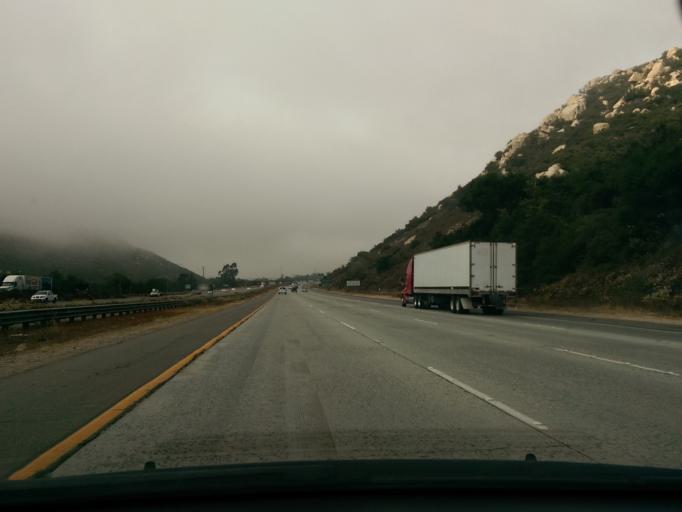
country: US
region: California
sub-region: San Diego County
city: Rainbow
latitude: 33.4452
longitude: -117.1369
